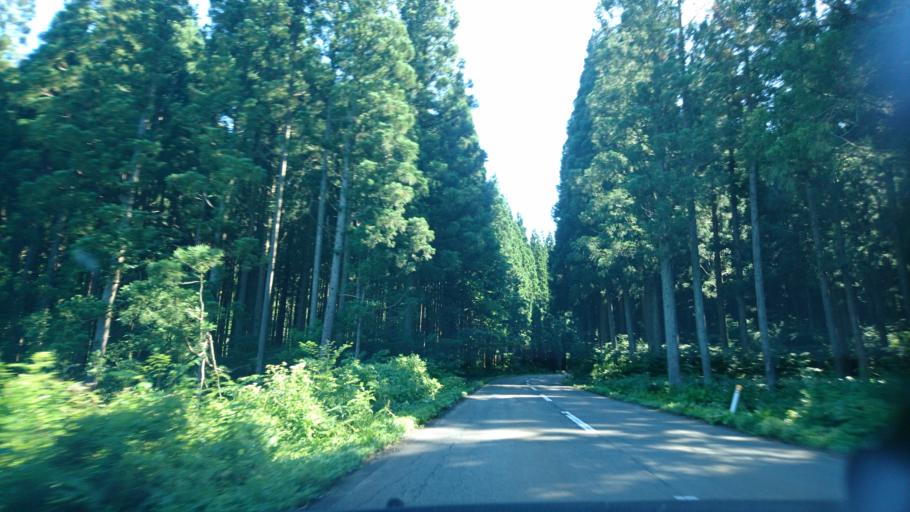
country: JP
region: Akita
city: Kakunodatemachi
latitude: 39.7088
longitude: 140.6073
